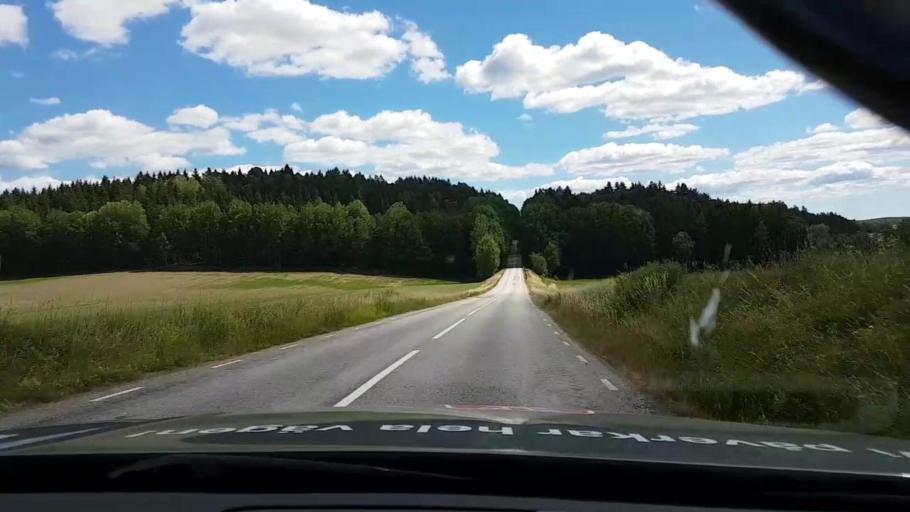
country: SE
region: Kalmar
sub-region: Vasterviks Kommun
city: Overum
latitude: 58.0683
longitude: 16.3918
